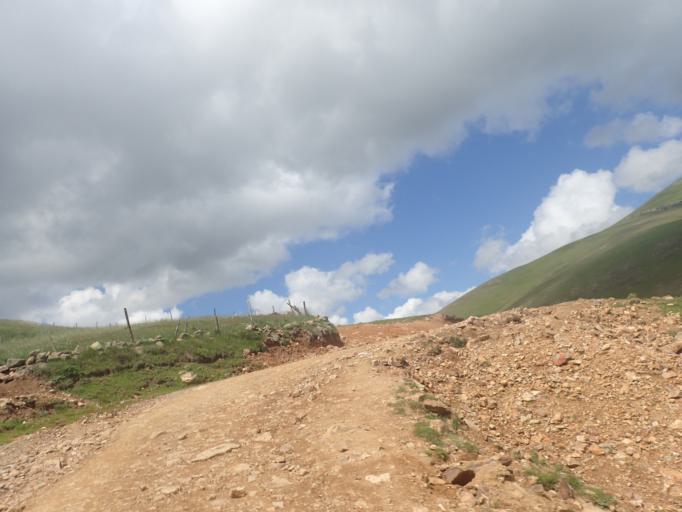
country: TR
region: Ordu
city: Yesilce
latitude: 40.5834
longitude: 37.9693
